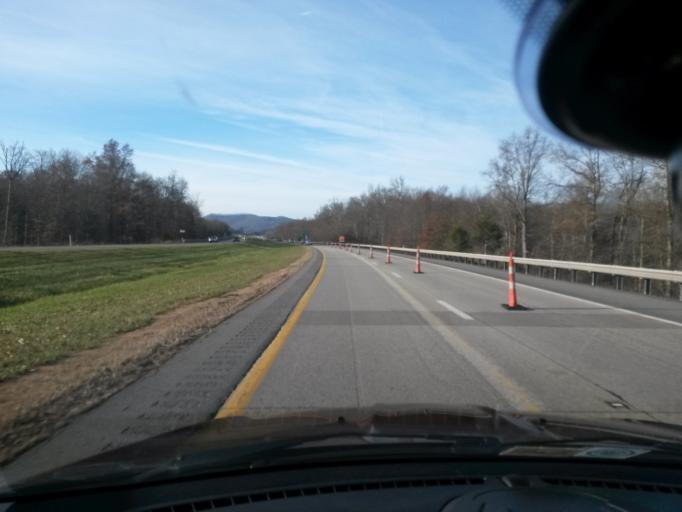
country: US
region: West Virginia
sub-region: Greenbrier County
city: Rainelle
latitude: 37.8643
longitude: -80.7120
